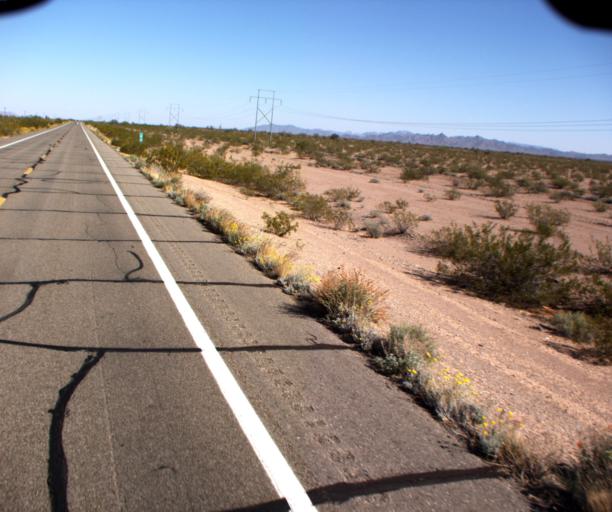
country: US
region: Arizona
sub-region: La Paz County
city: Quartzsite
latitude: 33.3685
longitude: -114.2171
